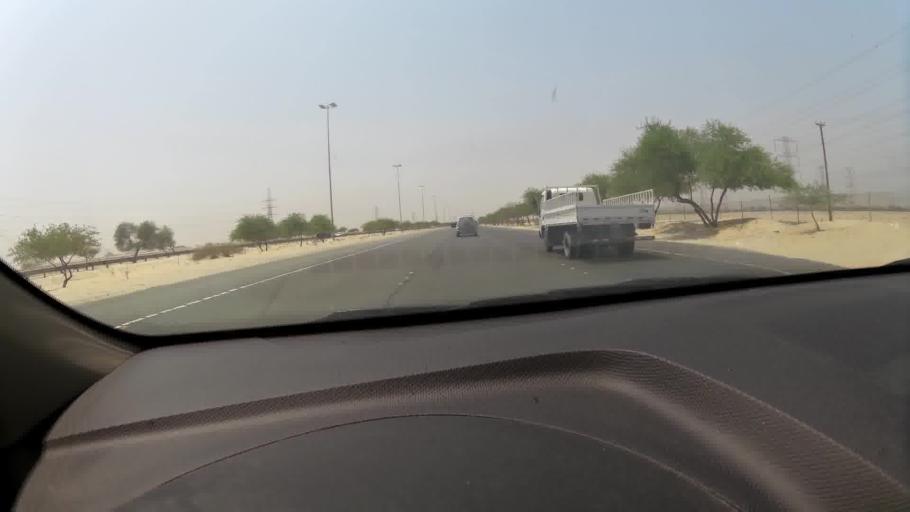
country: KW
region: Al Ahmadi
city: Al Fahahil
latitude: 28.9355
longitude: 48.1631
